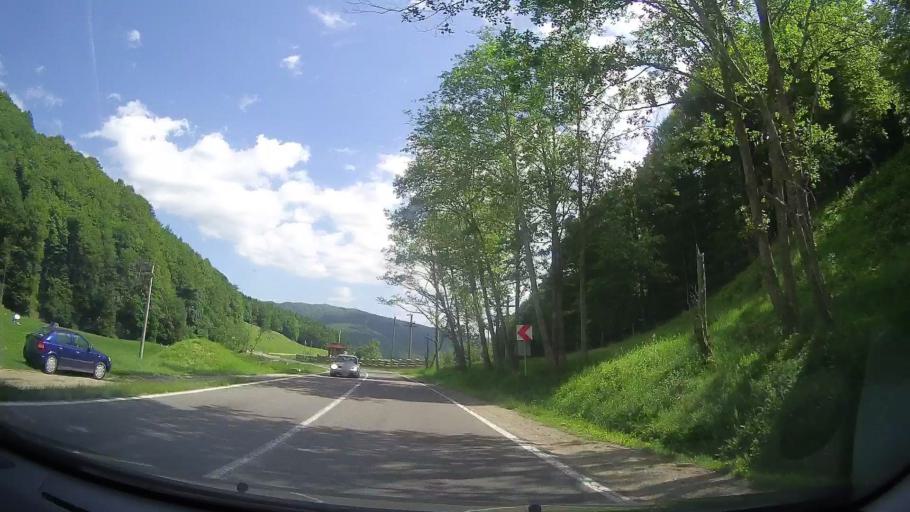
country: RO
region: Prahova
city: Maneciu
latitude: 45.4365
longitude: 25.9363
